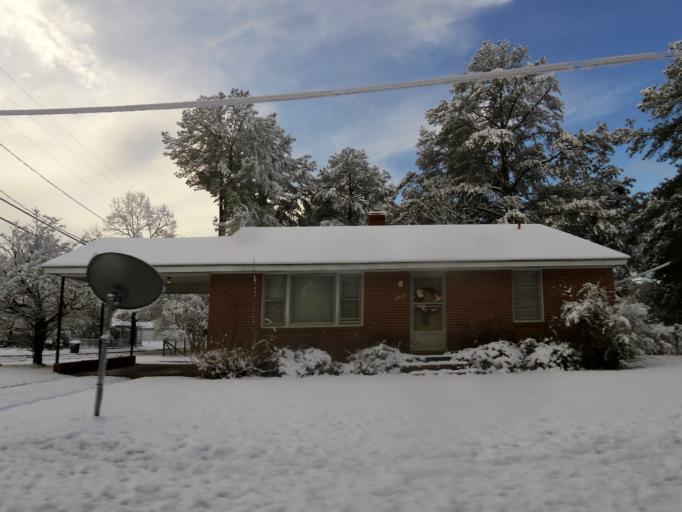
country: US
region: North Carolina
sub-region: Nash County
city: Rocky Mount
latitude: 35.9307
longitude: -77.8205
